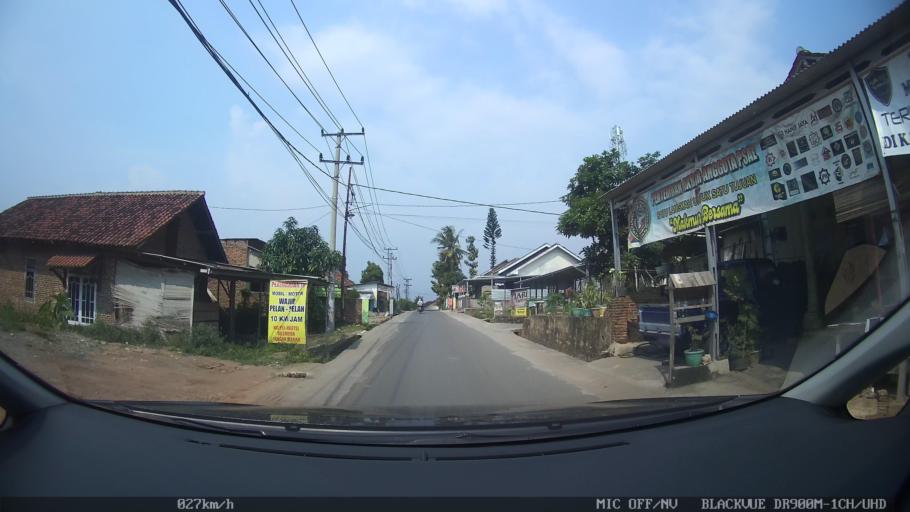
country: ID
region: Lampung
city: Natar
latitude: -5.3480
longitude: 105.2210
